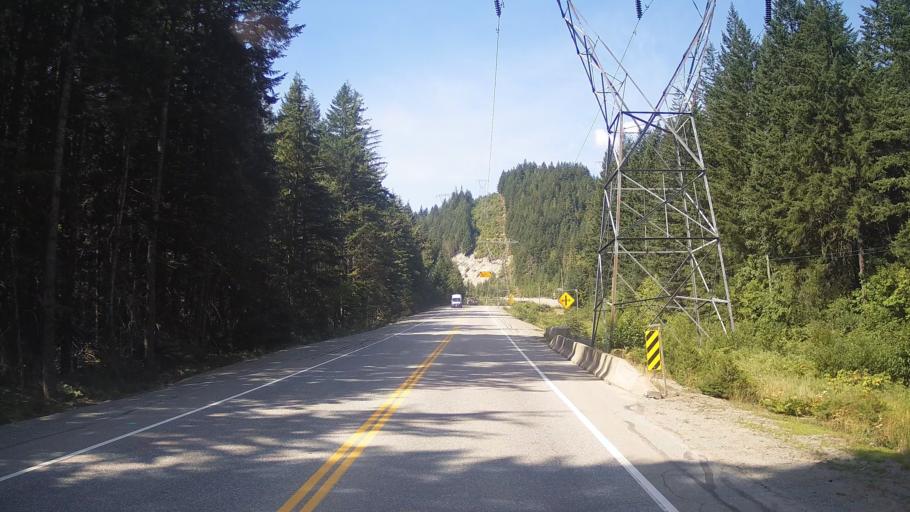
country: CA
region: British Columbia
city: Pemberton
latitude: 50.2947
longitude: -122.8273
